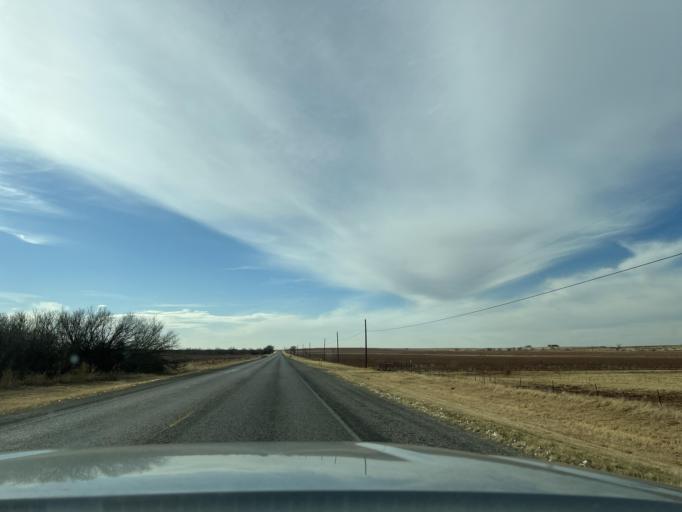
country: US
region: Texas
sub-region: Fisher County
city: Roby
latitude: 32.7411
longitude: -100.4726
